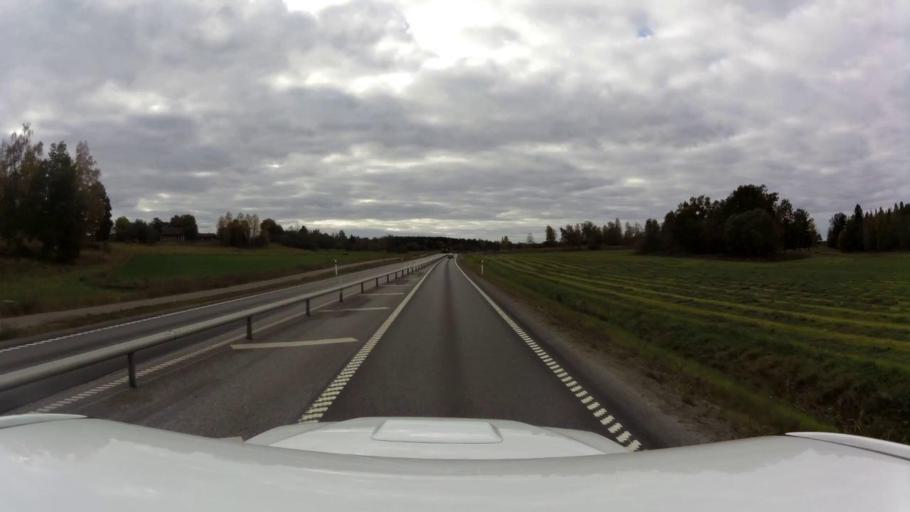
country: SE
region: OEstergoetland
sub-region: Linkopings Kommun
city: Malmslatt
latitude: 58.3137
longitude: 15.5672
